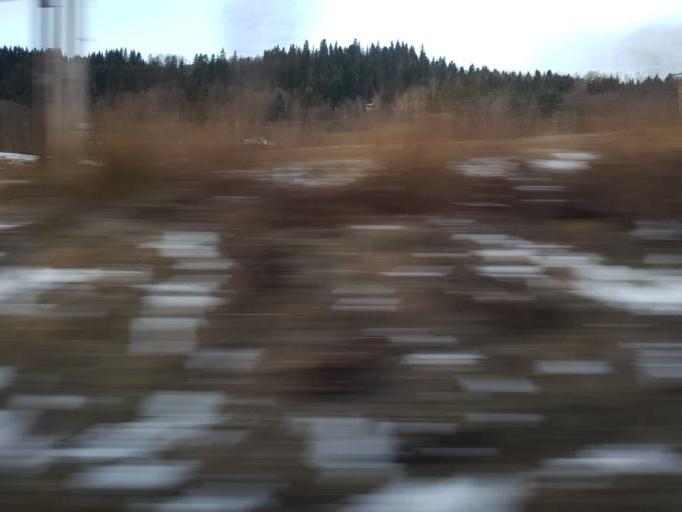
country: NO
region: Sor-Trondelag
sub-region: Midtre Gauldal
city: Storen
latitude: 62.9544
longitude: 10.1889
